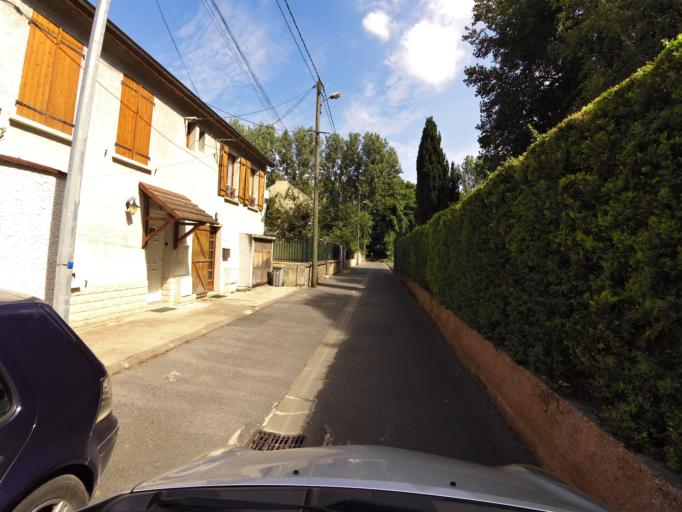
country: FR
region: Ile-de-France
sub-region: Departement de Seine-Saint-Denis
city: Gournay-sur-Marne
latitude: 48.8670
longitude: 2.5913
